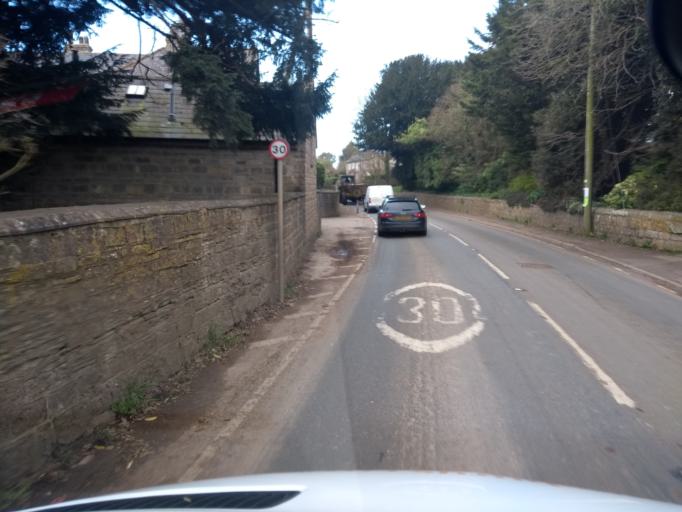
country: GB
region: England
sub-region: Somerset
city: Langport
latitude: 51.1240
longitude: -2.8393
